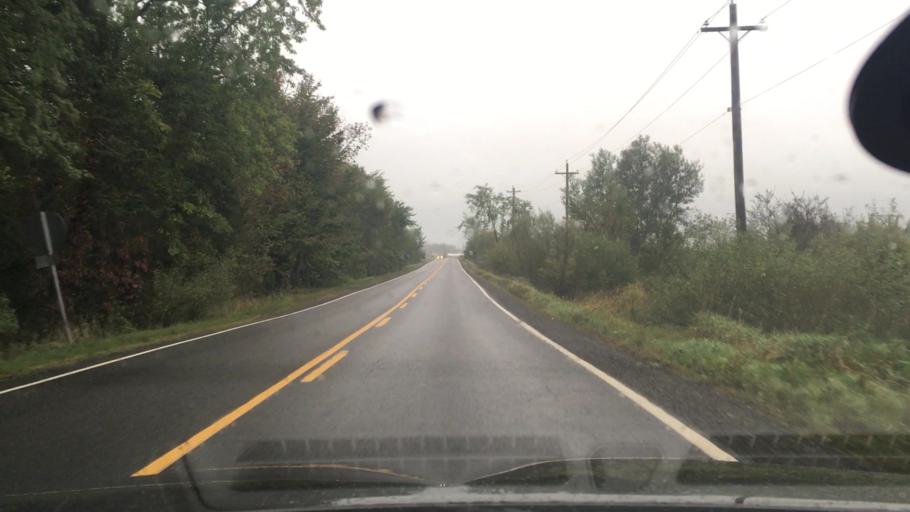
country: CA
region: Nova Scotia
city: Windsor
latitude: 44.9774
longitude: -64.1327
